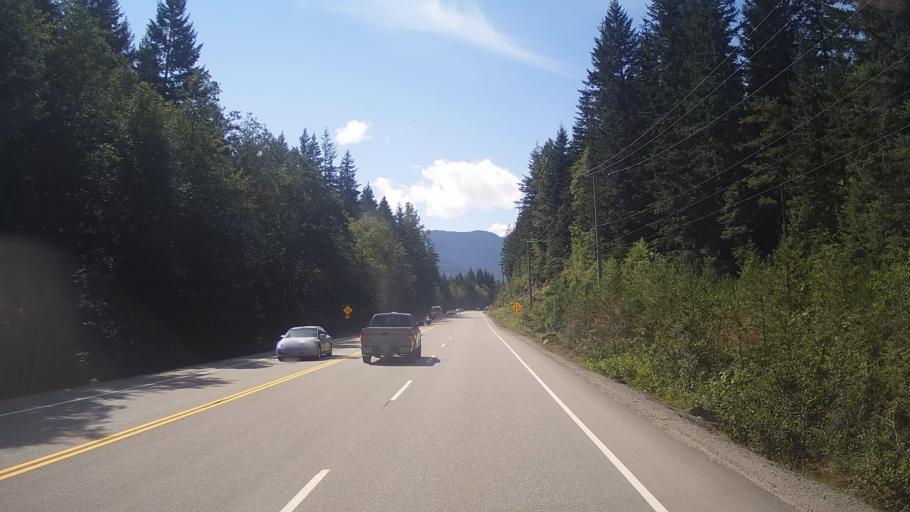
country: CA
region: British Columbia
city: Whistler
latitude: 50.2040
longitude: -122.8817
